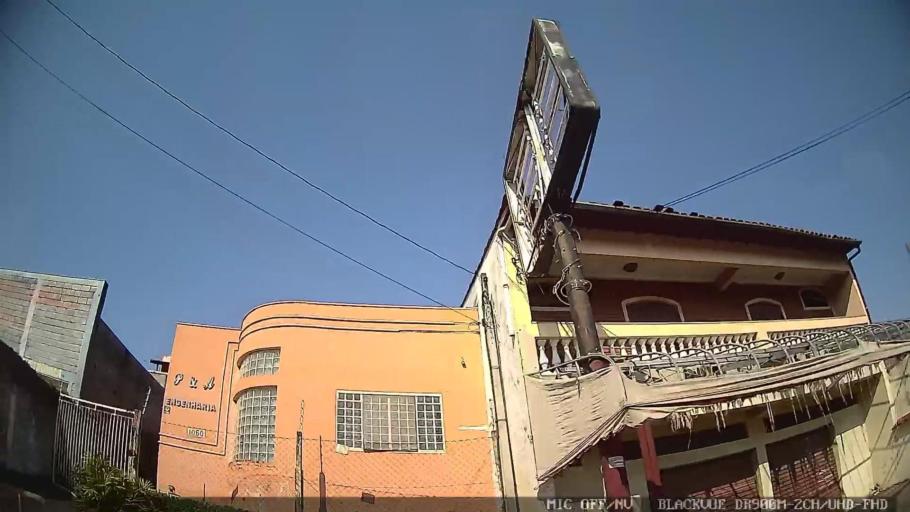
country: BR
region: Sao Paulo
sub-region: Itatiba
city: Itatiba
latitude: -22.9957
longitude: -46.8489
